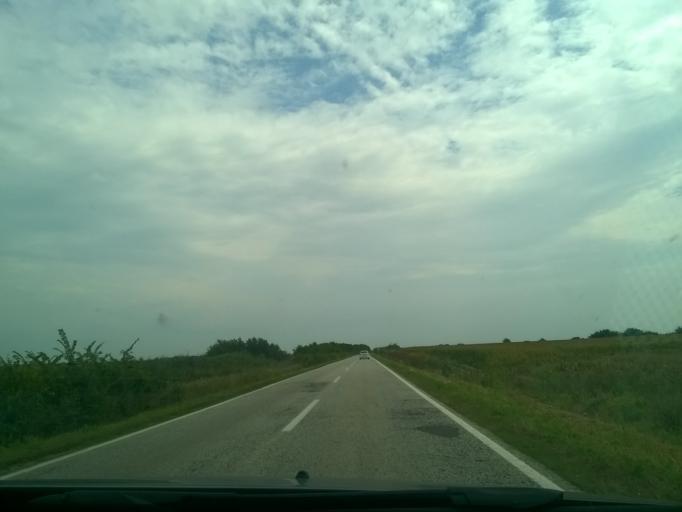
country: RS
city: Banatski Despotovac
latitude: 45.3873
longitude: 20.6203
